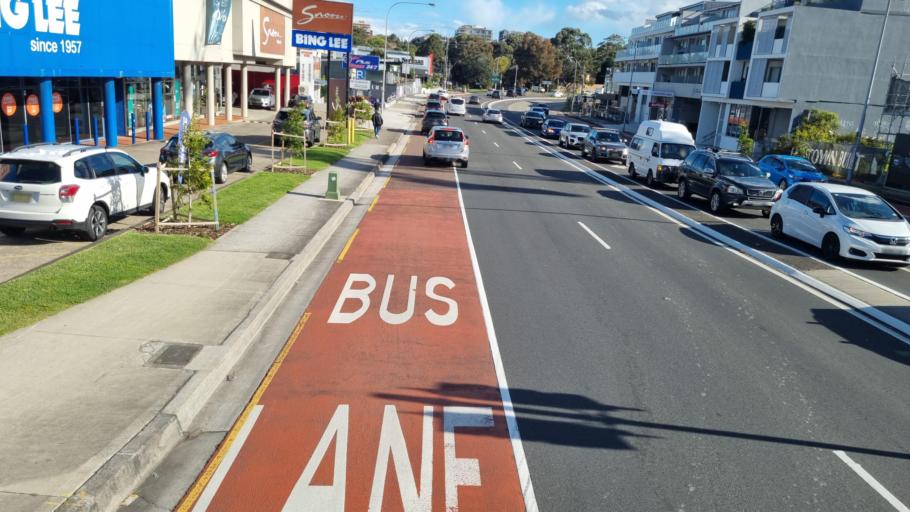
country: AU
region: New South Wales
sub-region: Warringah
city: North Manly
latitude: -33.7866
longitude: 151.2667
